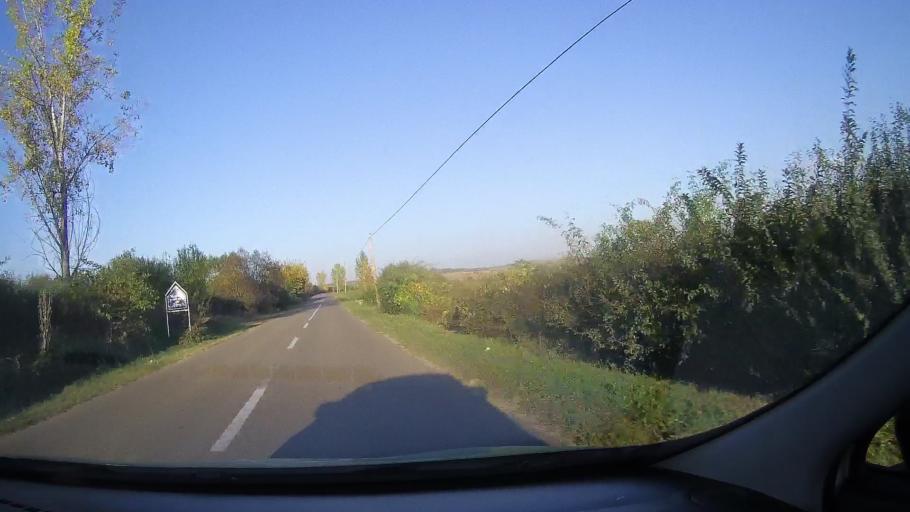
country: RO
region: Bihor
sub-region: Comuna Paleu
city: Paleu
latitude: 47.1277
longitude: 21.9701
